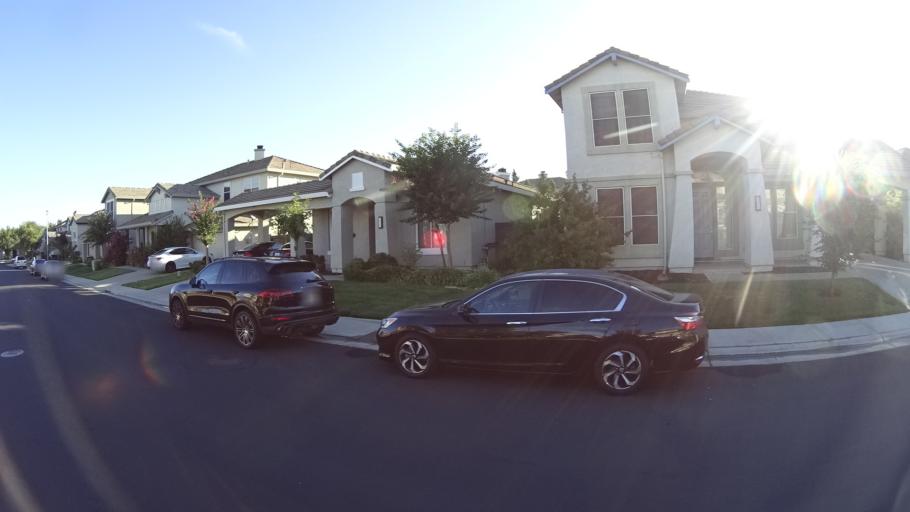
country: US
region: California
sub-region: Sacramento County
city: Laguna
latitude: 38.4003
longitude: -121.4798
